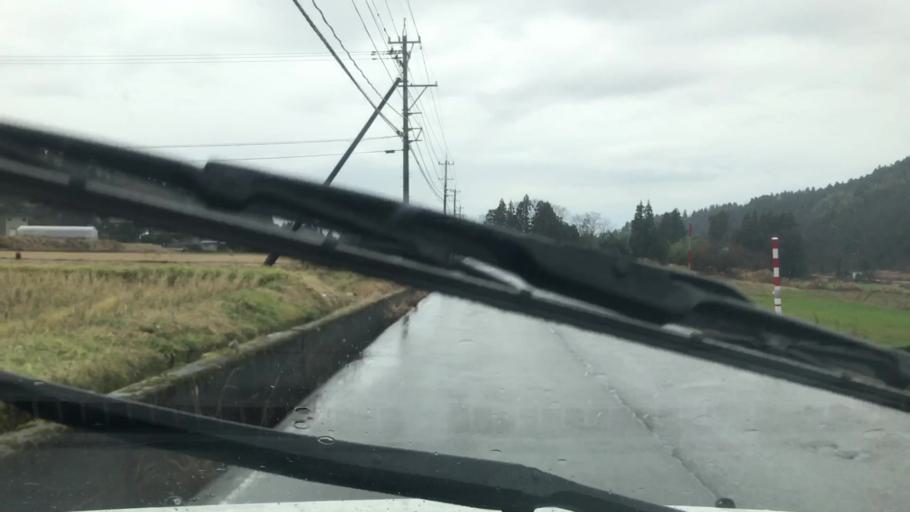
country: JP
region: Toyama
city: Kamiichi
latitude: 36.6003
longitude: 137.3001
